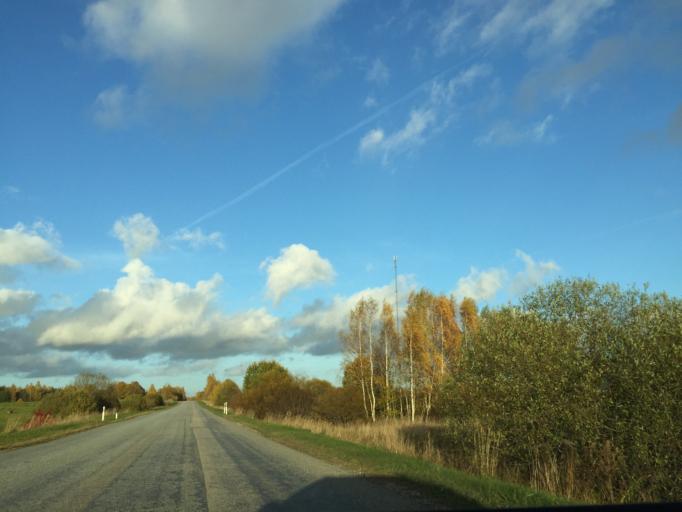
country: LV
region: Ogre
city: Jumprava
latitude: 56.7873
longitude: 25.0273
